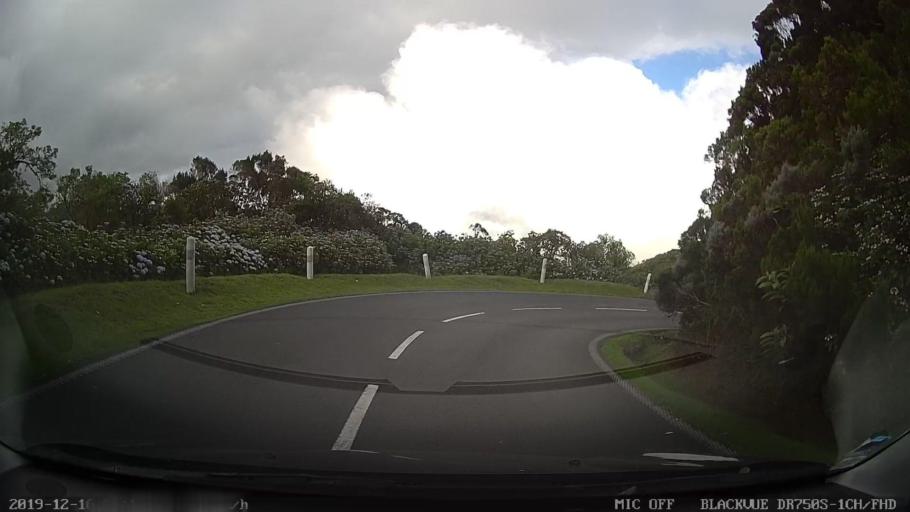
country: RE
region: Reunion
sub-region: Reunion
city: Cilaos
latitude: -21.1632
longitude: 55.5938
